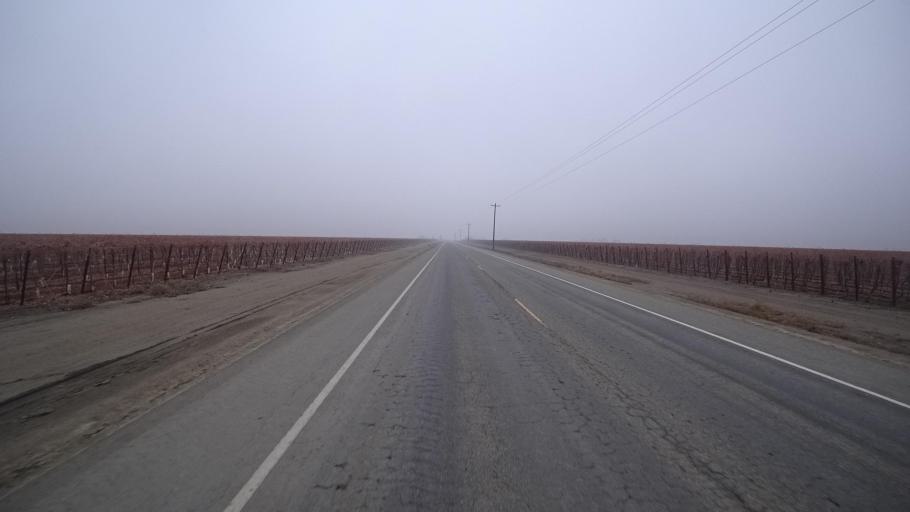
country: US
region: California
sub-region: Kern County
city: Buttonwillow
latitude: 35.4213
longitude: -119.5186
